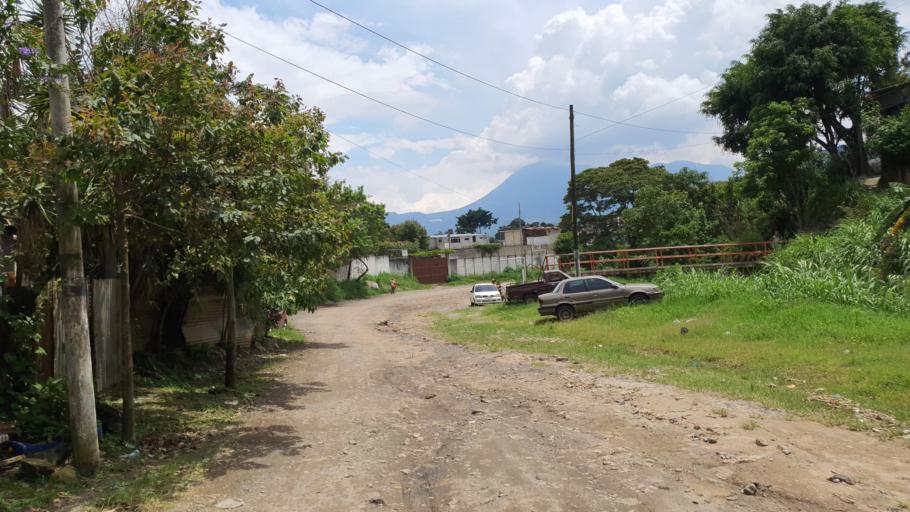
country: GT
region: Guatemala
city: Villa Canales
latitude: 14.4860
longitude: -90.5316
